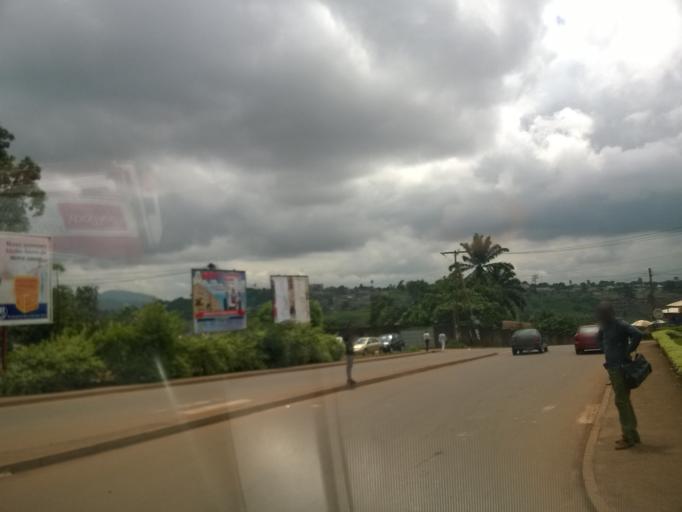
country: CM
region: Centre
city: Yaounde
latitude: 3.8445
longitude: 11.5016
